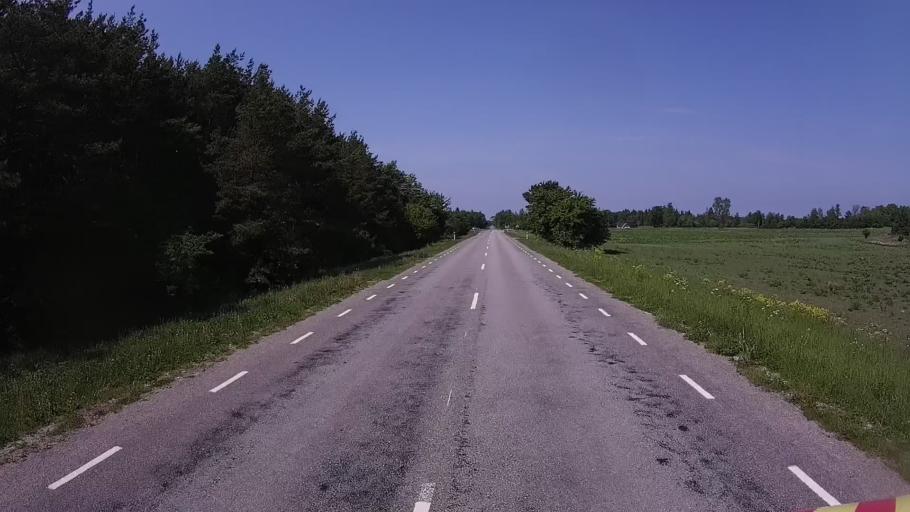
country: EE
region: Saare
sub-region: Kuressaare linn
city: Kuressaare
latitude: 58.3618
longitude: 22.0595
